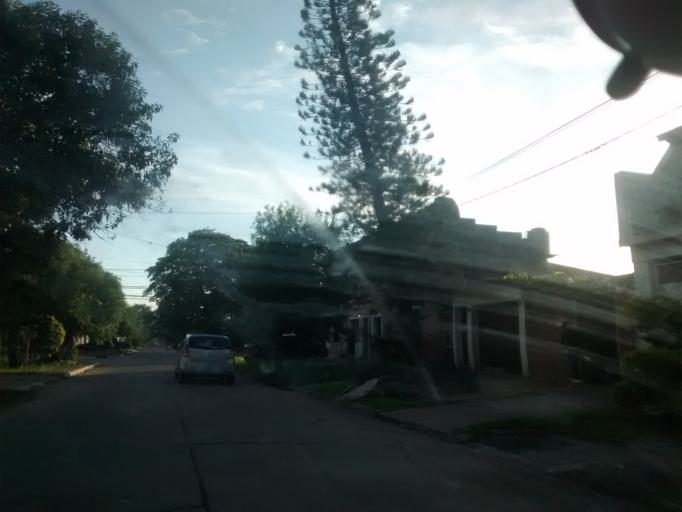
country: AR
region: Chaco
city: Resistencia
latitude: -27.4609
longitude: -58.9745
